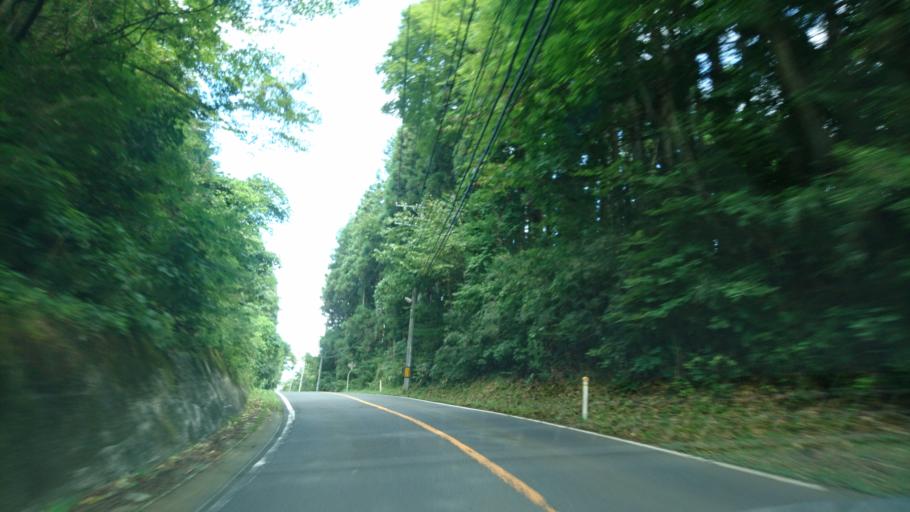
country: JP
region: Miyagi
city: Furukawa
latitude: 38.7811
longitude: 140.8514
